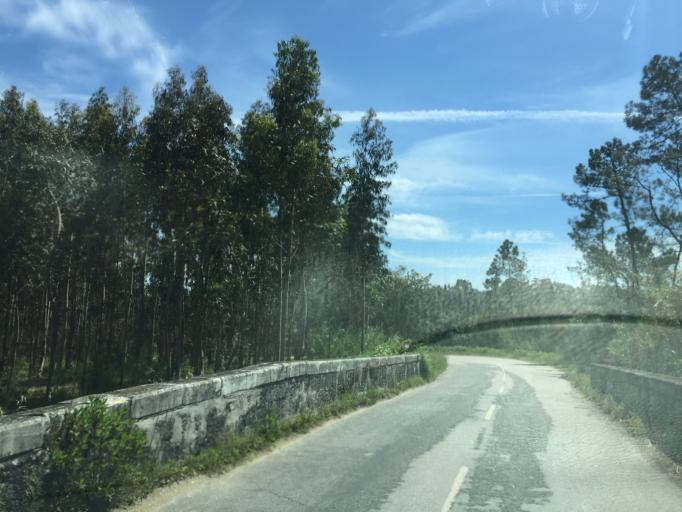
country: PT
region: Leiria
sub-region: Pombal
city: Lourical
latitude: 40.0682
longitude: -8.7606
